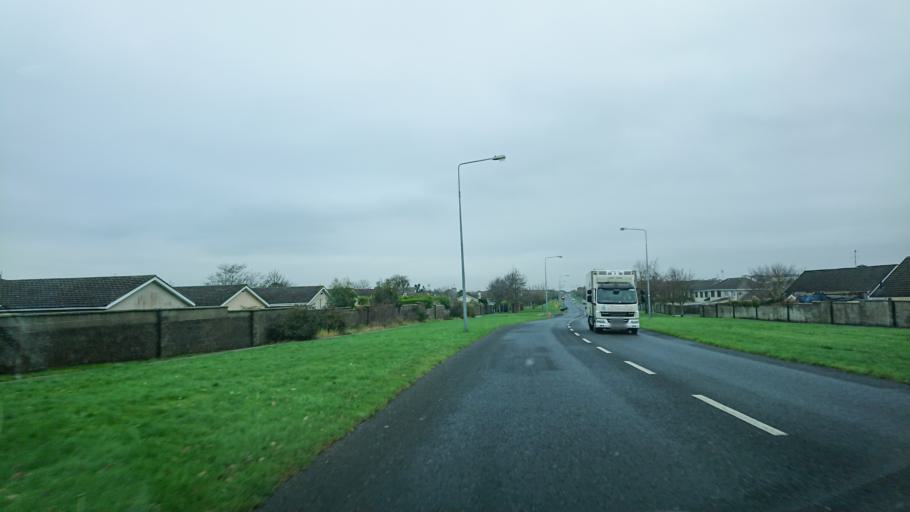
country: IE
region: Munster
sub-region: Waterford
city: Tra Mhor
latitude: 52.1593
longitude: -7.1690
